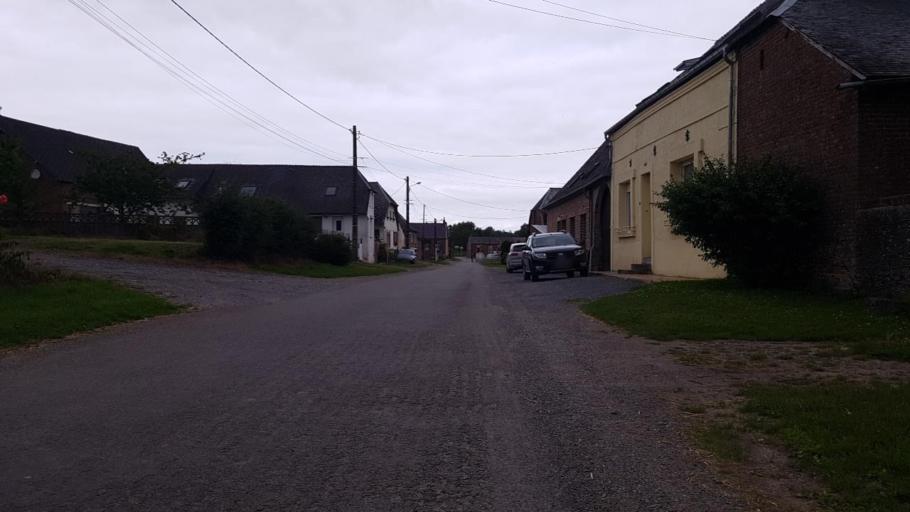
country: FR
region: Picardie
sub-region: Departement de l'Aisne
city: La Capelle
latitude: 49.9068
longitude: 3.8917
